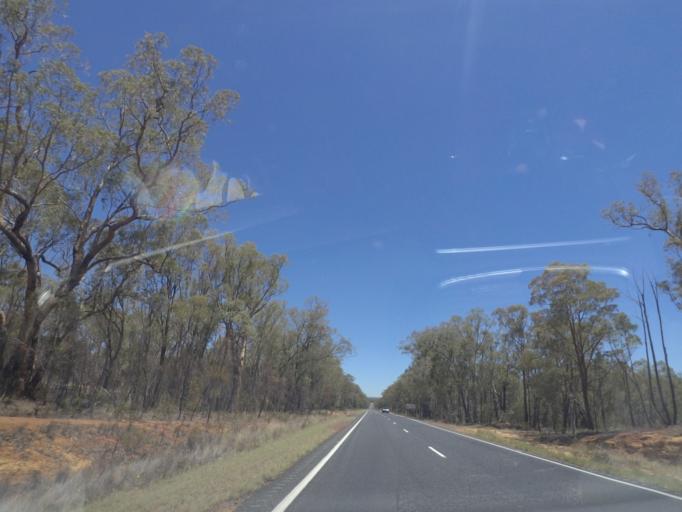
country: AU
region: New South Wales
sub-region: Warrumbungle Shire
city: Coonabarabran
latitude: -31.2147
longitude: 149.3282
